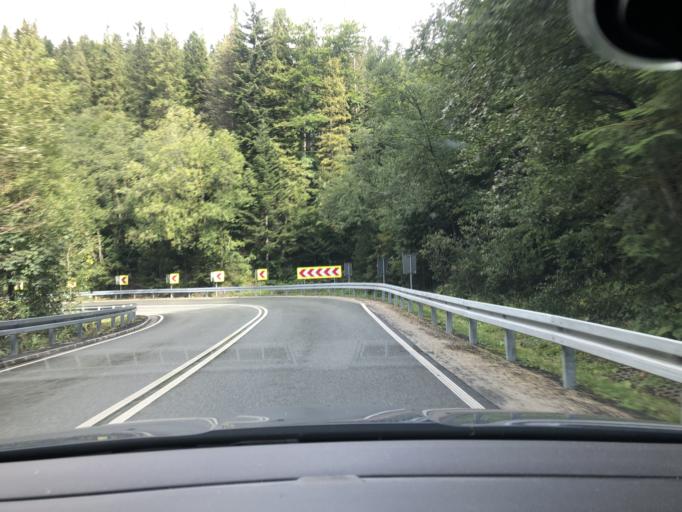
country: PL
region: Lesser Poland Voivodeship
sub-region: Powiat suski
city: Zawoja
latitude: 49.5966
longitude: 19.5862
